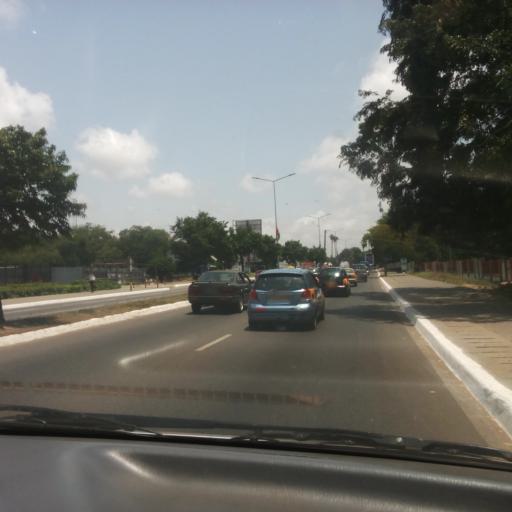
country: GH
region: Greater Accra
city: Accra
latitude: 5.5573
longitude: -0.1988
